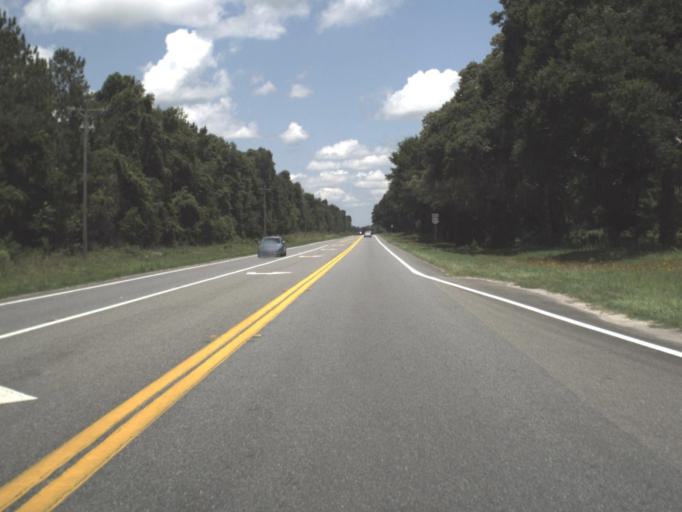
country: US
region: Florida
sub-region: Alachua County
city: High Springs
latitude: 29.8855
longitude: -82.6689
